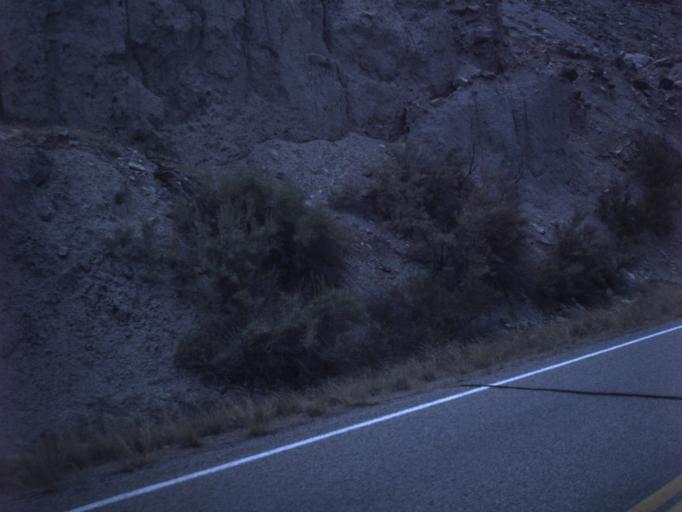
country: US
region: Utah
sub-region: Grand County
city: Moab
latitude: 38.8349
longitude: -109.2878
